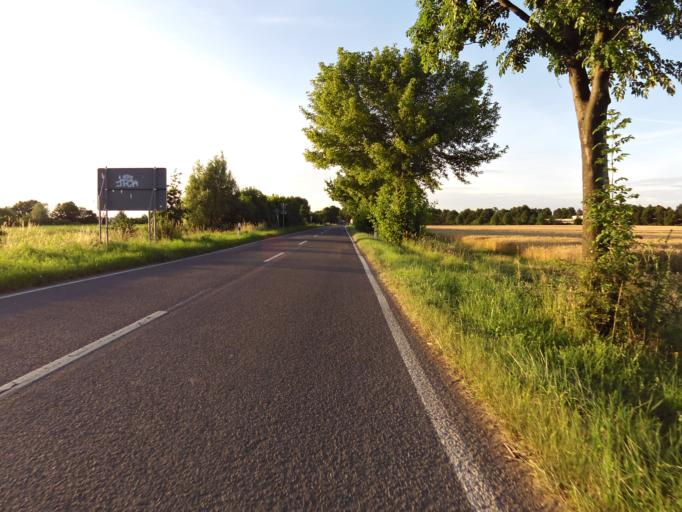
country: DE
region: Rheinland-Pfalz
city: Hessheim
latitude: 49.5592
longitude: 8.3056
